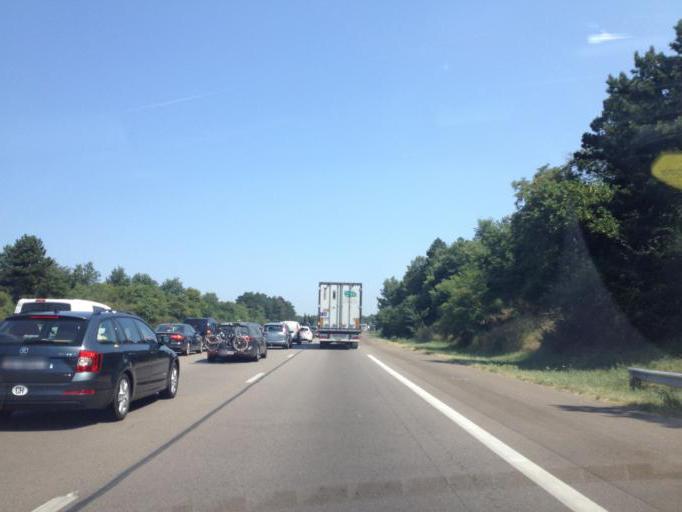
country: FR
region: Rhone-Alpes
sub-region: Departement de la Drome
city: Malataverne
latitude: 44.4960
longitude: 4.7676
